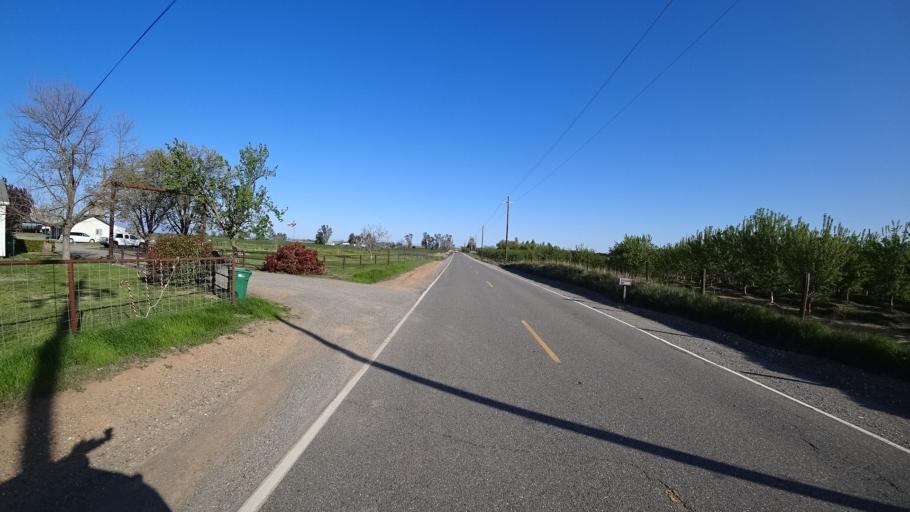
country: US
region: California
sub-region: Glenn County
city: Orland
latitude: 39.7634
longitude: -122.1072
